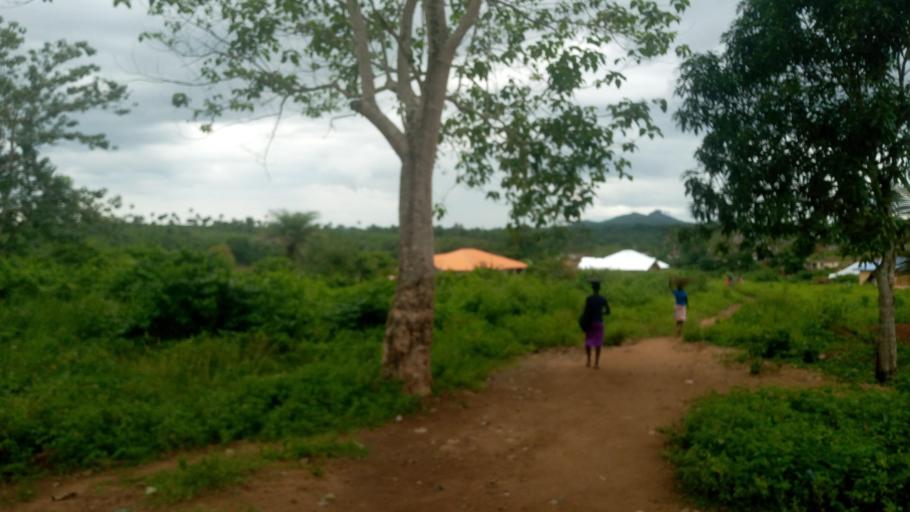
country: SL
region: Southern Province
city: Mogbwemo
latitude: 7.6014
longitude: -12.1780
